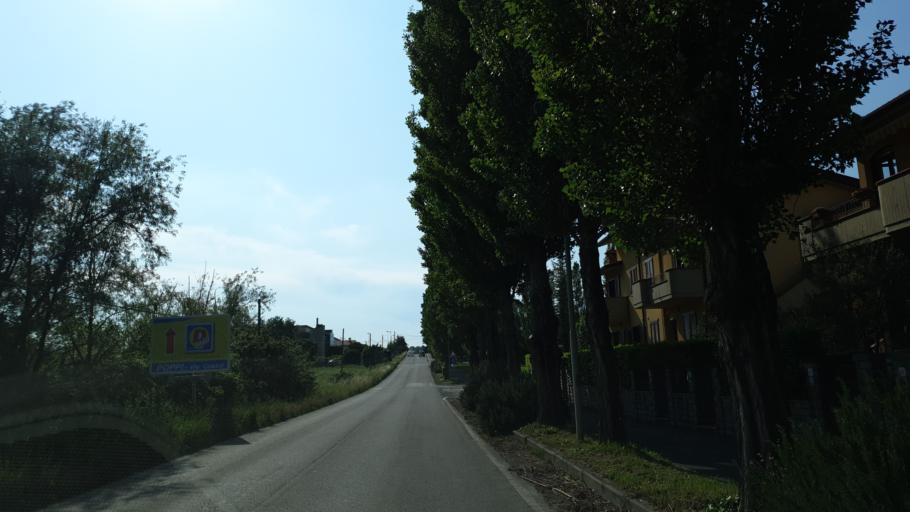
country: IT
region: Tuscany
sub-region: Province of Arezzo
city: Soci
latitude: 43.7375
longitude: 11.8075
